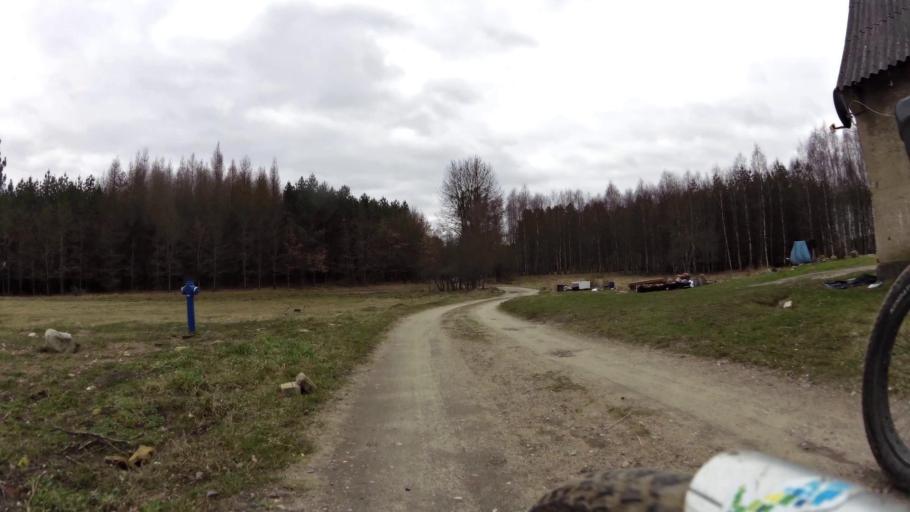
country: PL
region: Pomeranian Voivodeship
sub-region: Powiat bytowski
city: Trzebielino
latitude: 54.1185
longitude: 17.1288
